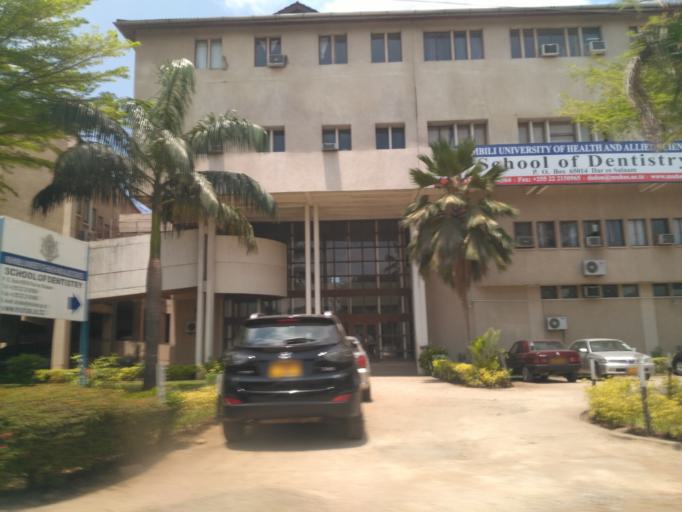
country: TZ
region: Dar es Salaam
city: Dar es Salaam
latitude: -6.8048
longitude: 39.2737
